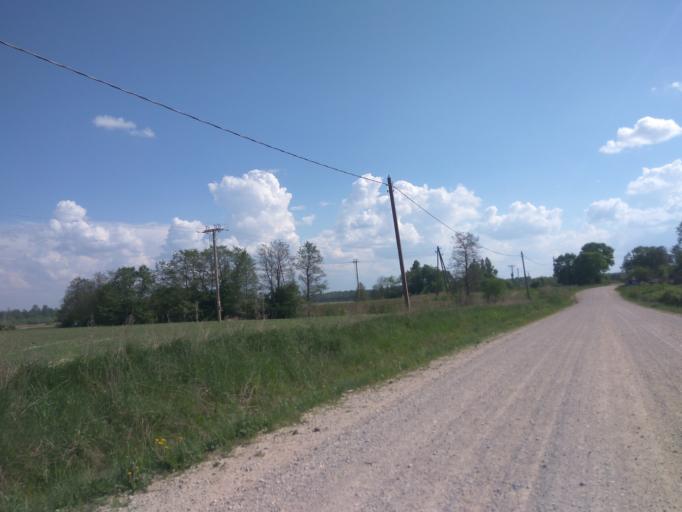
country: LV
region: Kuldigas Rajons
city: Kuldiga
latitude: 57.1619
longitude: 22.0186
